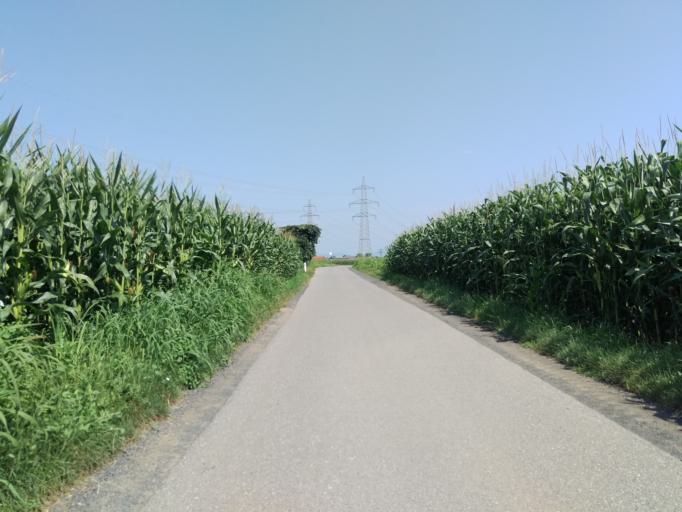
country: AT
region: Styria
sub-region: Politischer Bezirk Graz-Umgebung
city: Werndorf
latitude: 46.9312
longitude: 15.4898
